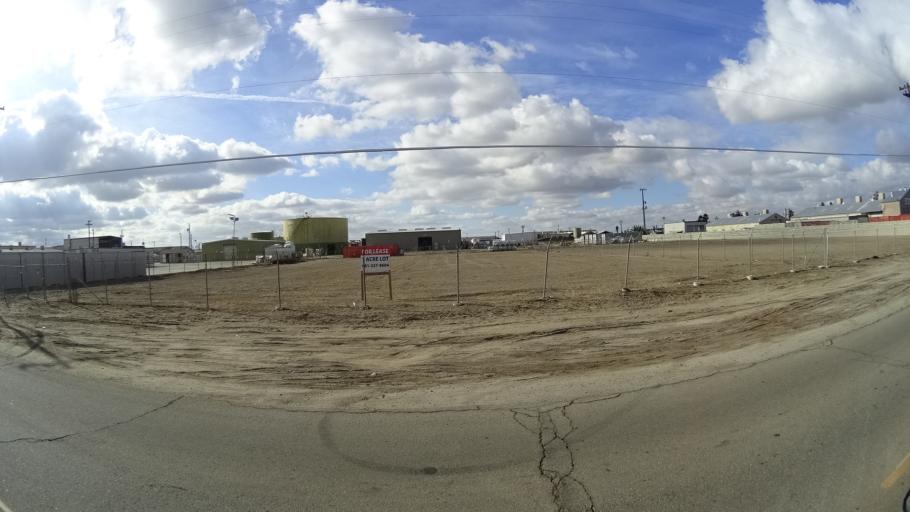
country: US
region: California
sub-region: Kern County
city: Bakersfield
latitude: 35.3592
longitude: -118.9720
